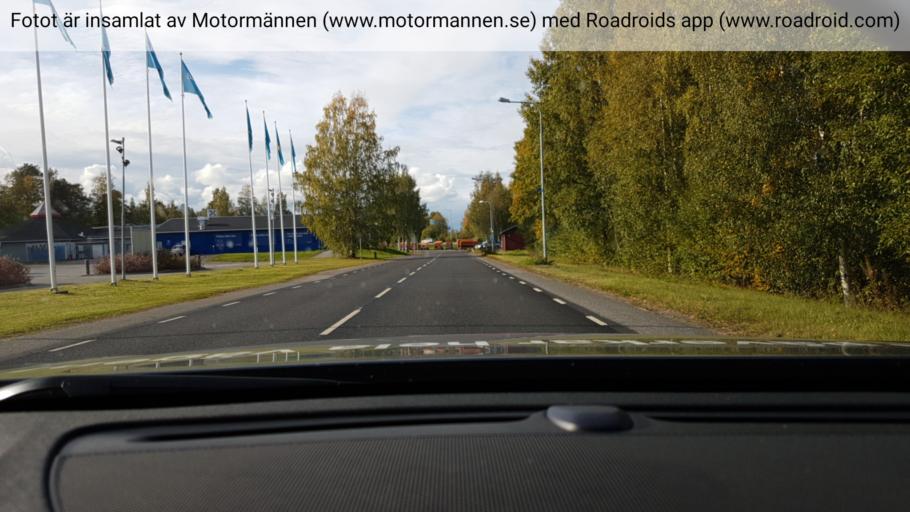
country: SE
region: Norrbotten
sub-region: Lulea Kommun
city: Bergnaset
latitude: 65.6137
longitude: 22.1064
